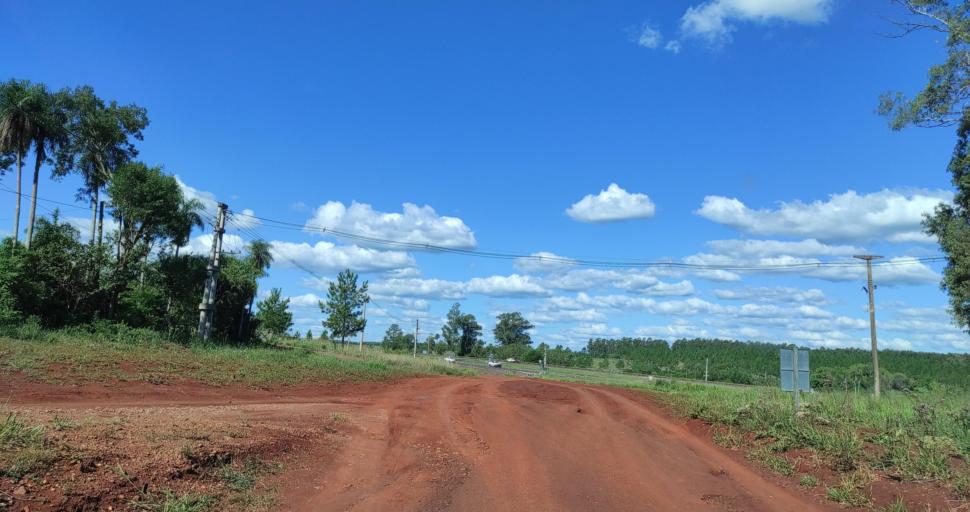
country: AR
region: Misiones
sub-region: Departamento de Candelaria
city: Candelaria
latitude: -27.4651
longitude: -55.7124
